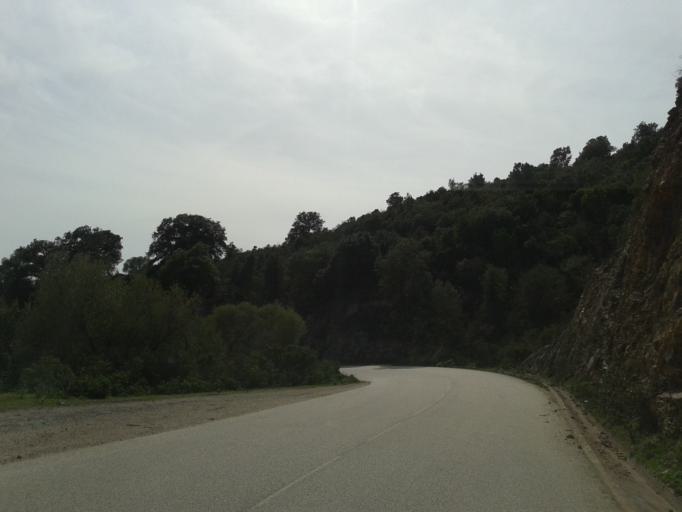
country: FR
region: Corsica
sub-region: Departement de la Haute-Corse
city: Monticello
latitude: 42.6566
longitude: 9.1153
